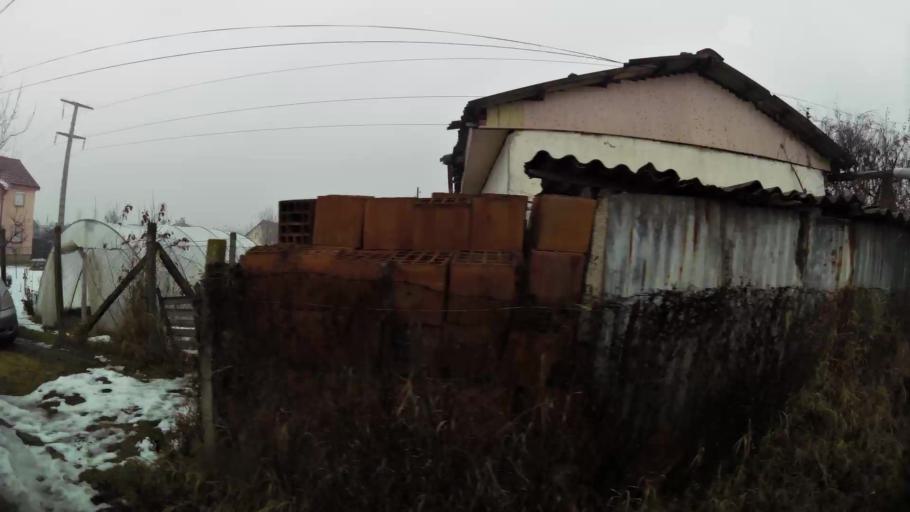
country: MK
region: Petrovec
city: Petrovec
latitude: 41.9350
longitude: 21.6124
